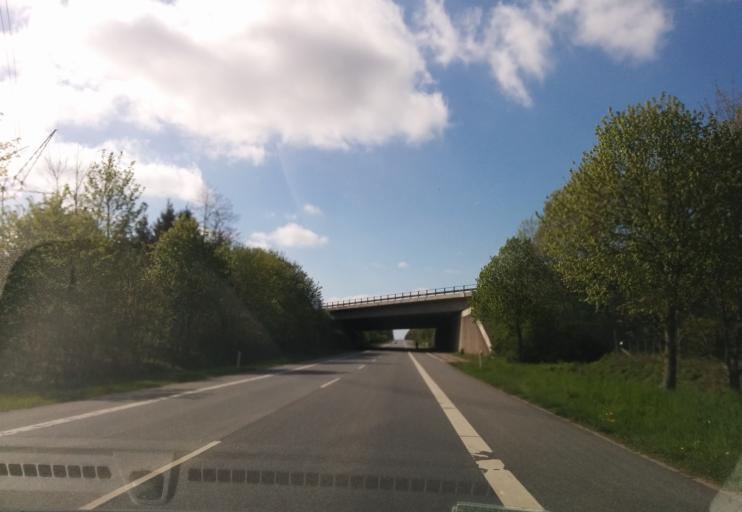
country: DK
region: South Denmark
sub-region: Assens Kommune
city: Arup
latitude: 55.4096
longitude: 10.0685
